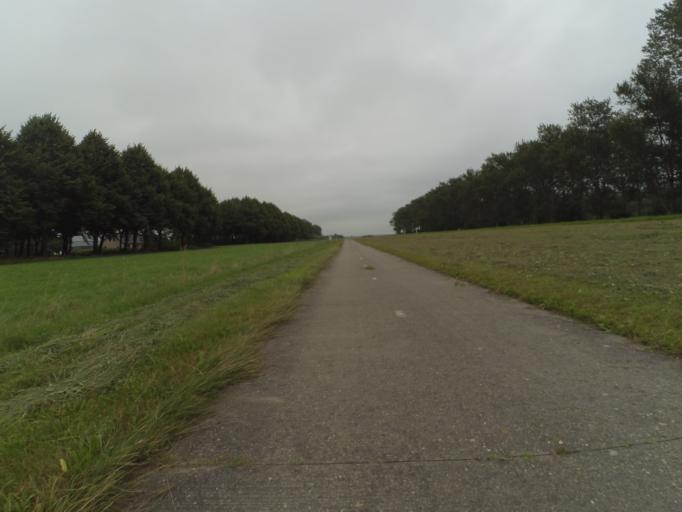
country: NL
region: Flevoland
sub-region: Gemeente Lelystad
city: Lelystad
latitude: 52.4204
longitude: 5.5104
